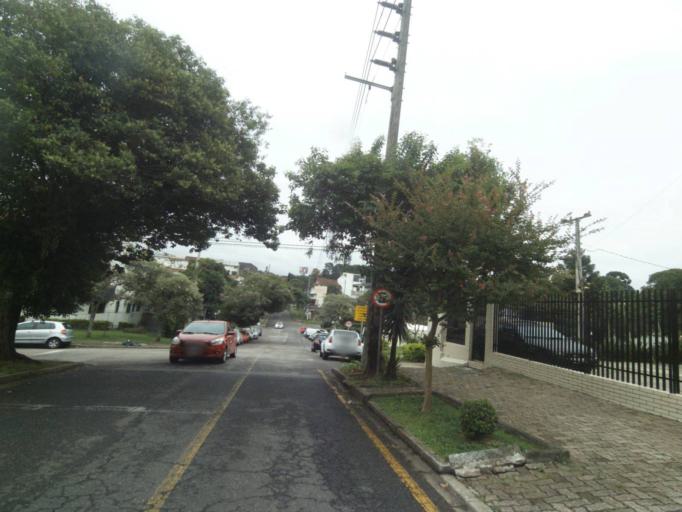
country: BR
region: Parana
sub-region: Curitiba
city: Curitiba
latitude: -25.4170
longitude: -49.2920
